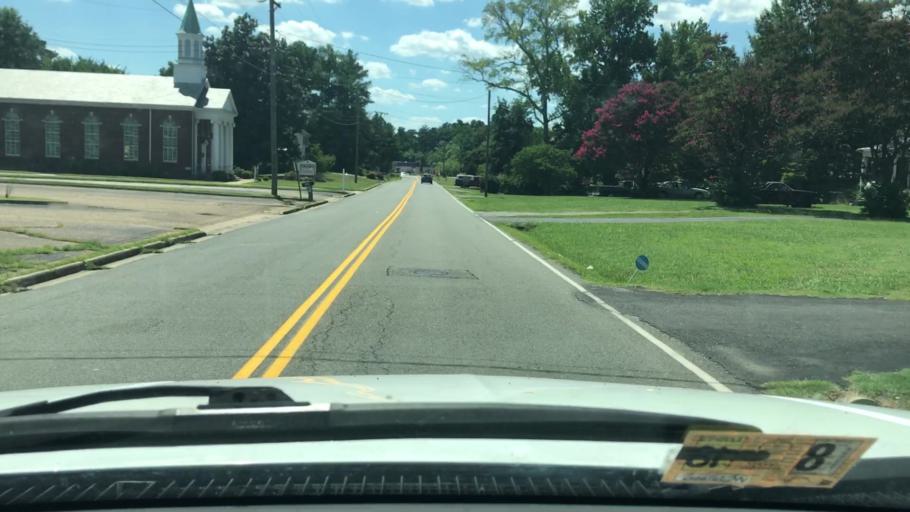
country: US
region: Virginia
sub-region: Henrico County
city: East Highland Park
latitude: 37.5702
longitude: -77.3973
